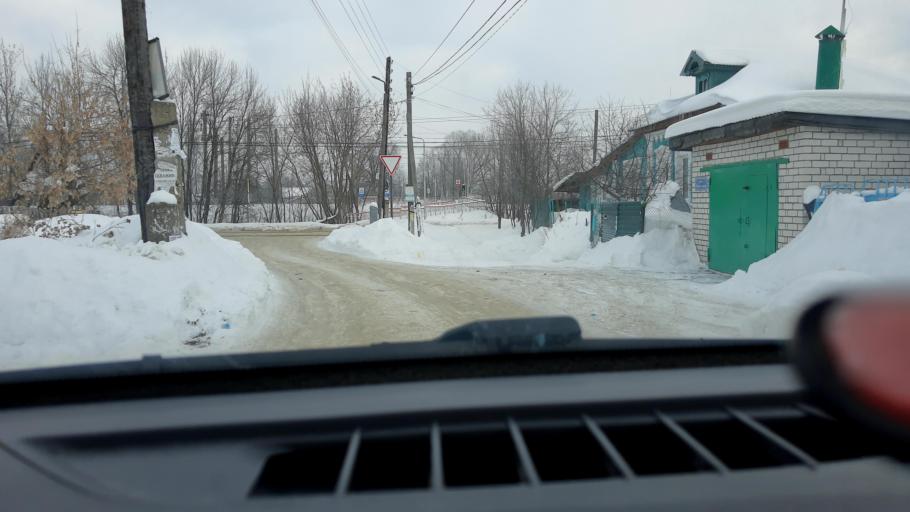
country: RU
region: Nizjnij Novgorod
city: Gorbatovka
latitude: 56.2625
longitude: 43.7367
